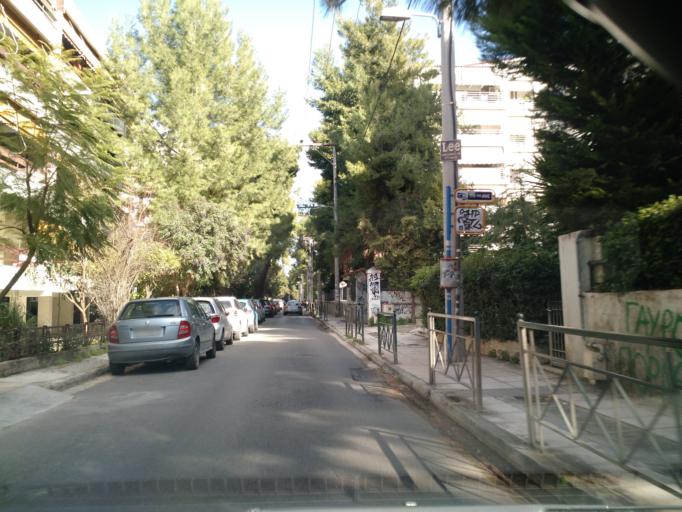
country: GR
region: Attica
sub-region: Nomarchia Athinas
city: Agia Paraskevi
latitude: 38.0072
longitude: 23.8285
